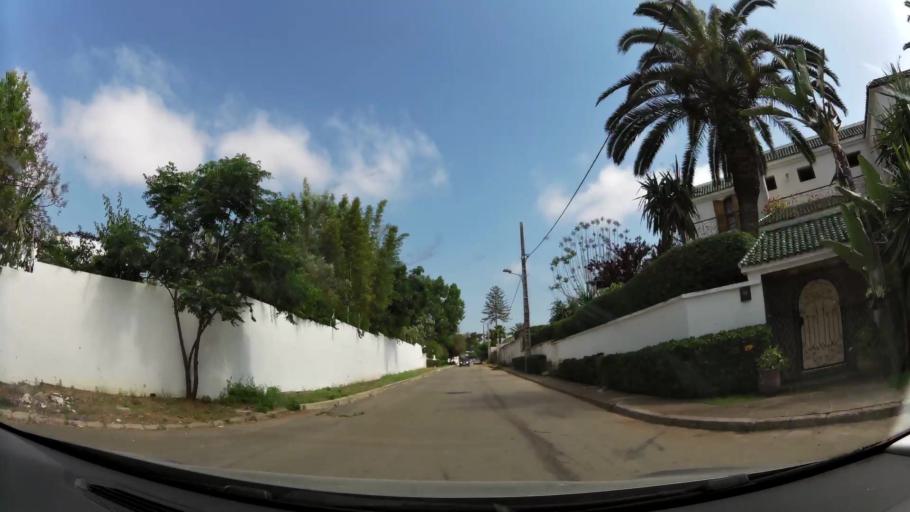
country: MA
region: Rabat-Sale-Zemmour-Zaer
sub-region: Rabat
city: Rabat
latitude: 33.9803
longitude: -6.8378
